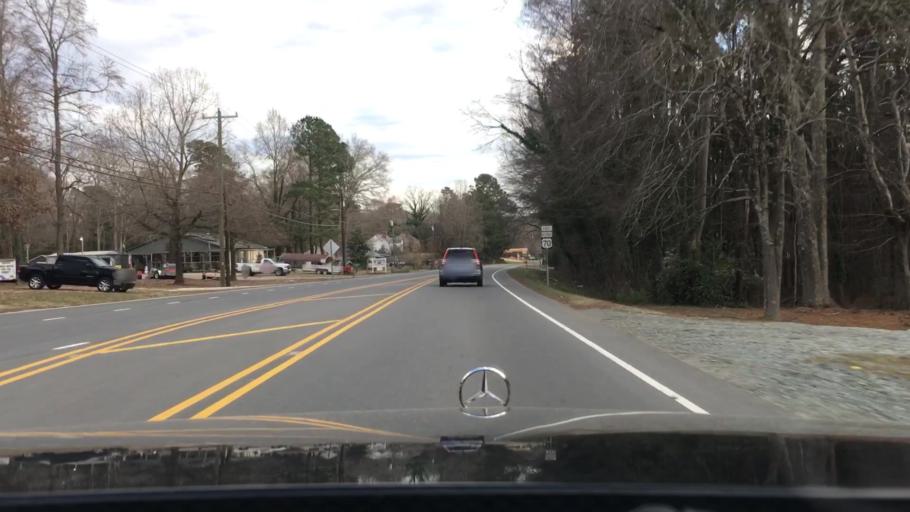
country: US
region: North Carolina
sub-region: Orange County
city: Hillsborough
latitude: 36.0816
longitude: -79.0789
